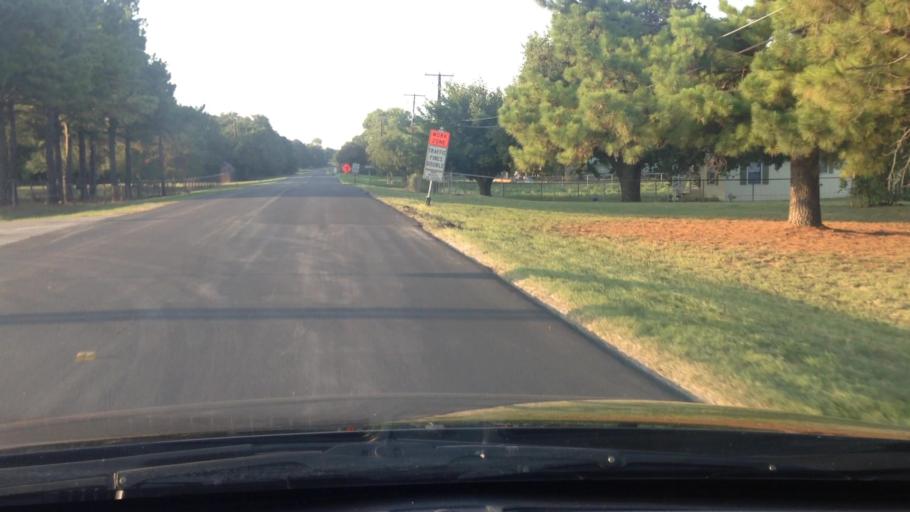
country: US
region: Texas
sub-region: Tarrant County
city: Rendon
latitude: 32.5983
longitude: -97.2502
